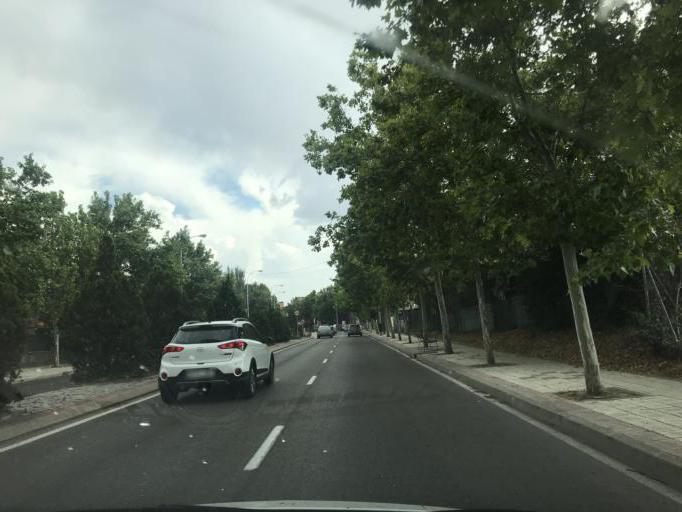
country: ES
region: Madrid
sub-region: Provincia de Madrid
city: Barajas de Madrid
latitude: 40.4770
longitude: -3.5820
